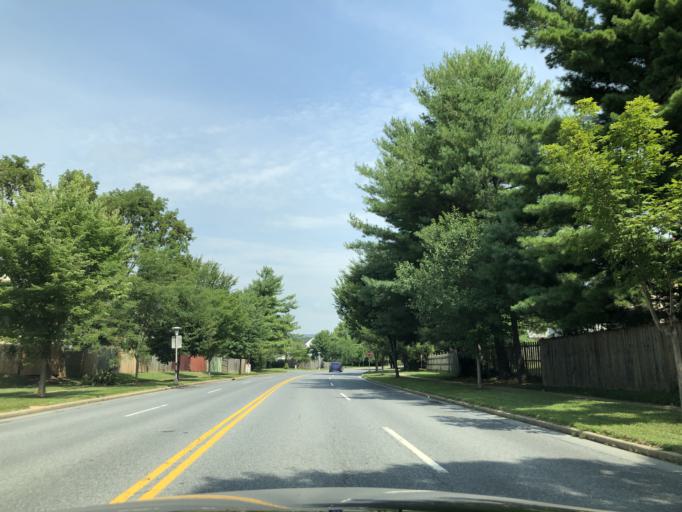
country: US
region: Maryland
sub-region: Frederick County
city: Clover Hill
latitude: 39.4253
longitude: -77.4482
